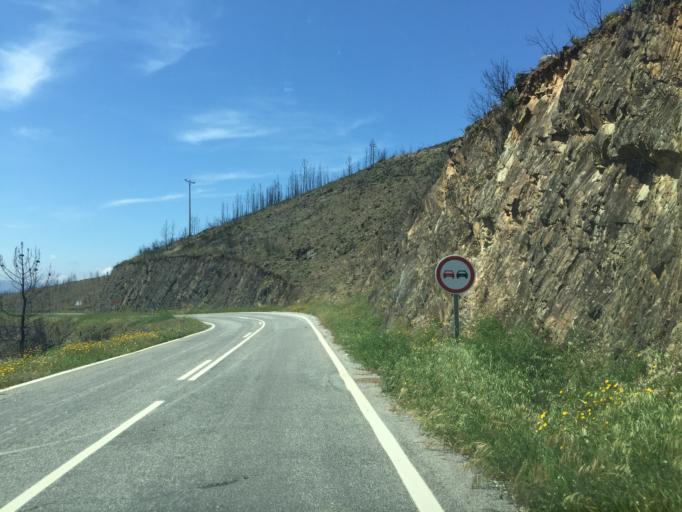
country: PT
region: Coimbra
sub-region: Pampilhosa da Serra
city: Pampilhosa da Serra
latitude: 40.0195
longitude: -7.9653
